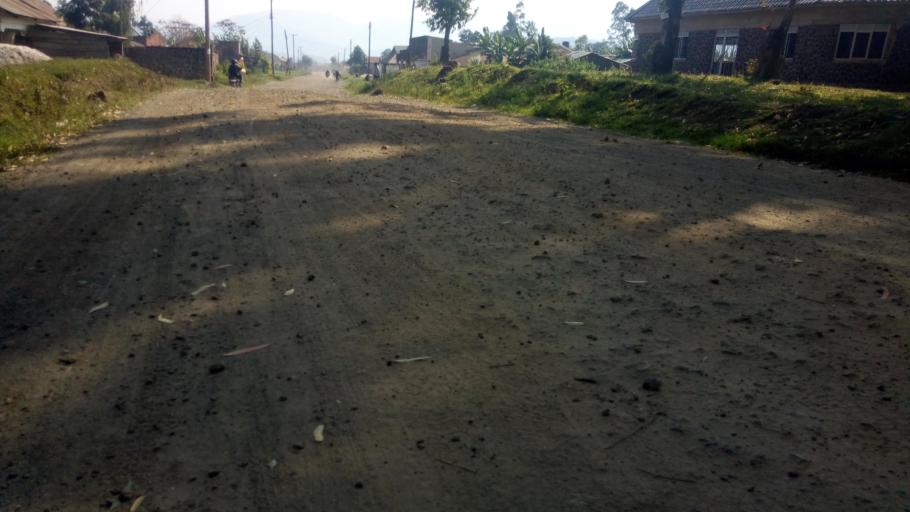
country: UG
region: Western Region
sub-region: Kisoro District
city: Kisoro
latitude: -1.2482
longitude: 29.7131
